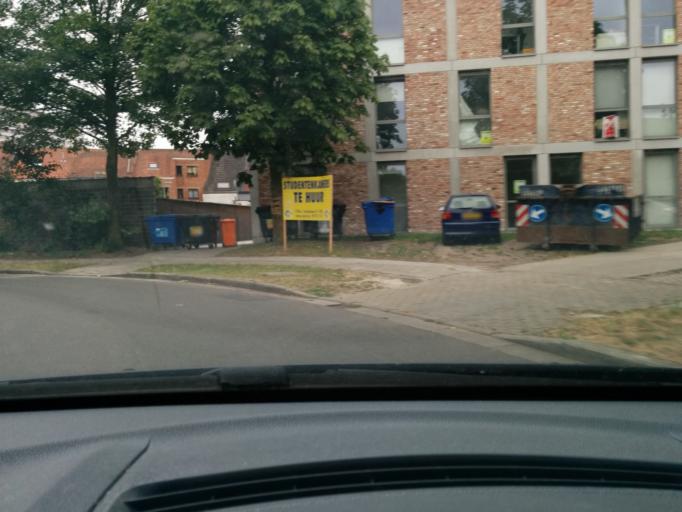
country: BE
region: Flanders
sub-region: Provincie Oost-Vlaanderen
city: Gent
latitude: 51.0562
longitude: 3.7008
